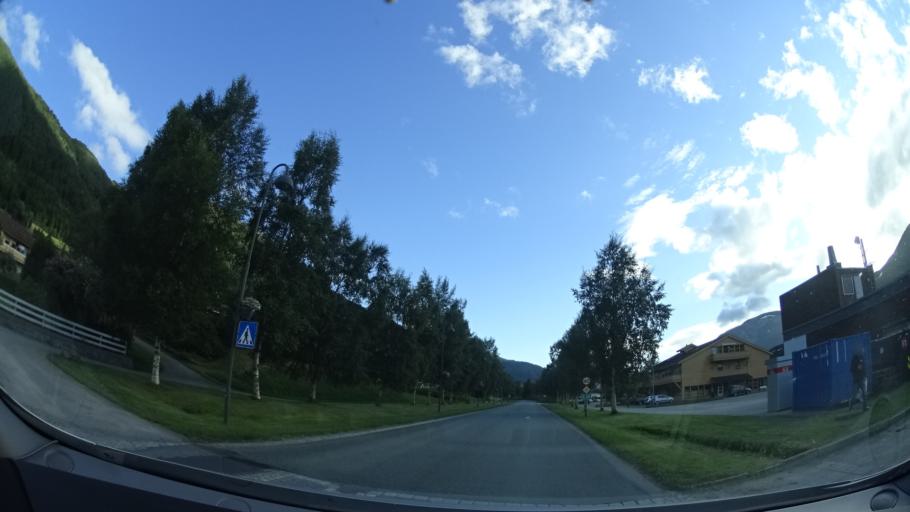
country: NO
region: More og Romsdal
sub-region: Gjemnes
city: Batnfjordsora
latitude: 62.8929
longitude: 7.6820
